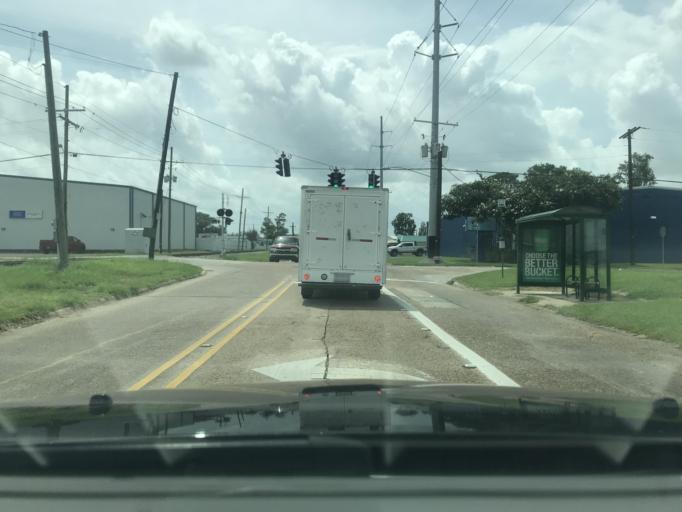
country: US
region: Louisiana
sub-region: Calcasieu Parish
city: Lake Charles
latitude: 30.2132
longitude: -93.2137
